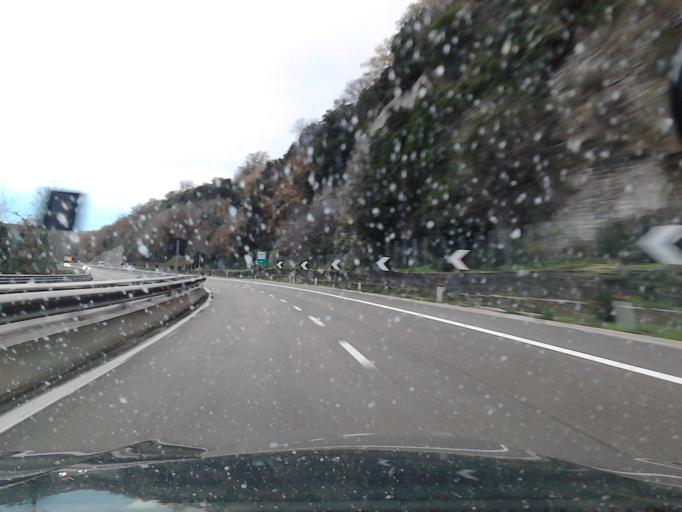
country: IT
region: Abruzzo
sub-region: Provincia di Chieti
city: San Vito Chietino
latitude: 42.2741
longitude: 14.4356
